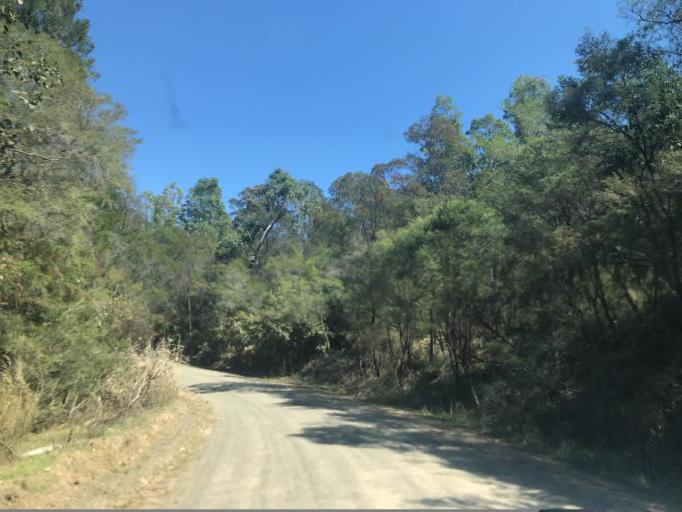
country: AU
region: New South Wales
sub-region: Wyong Shire
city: Little Jilliby
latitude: -33.1935
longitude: 151.0122
